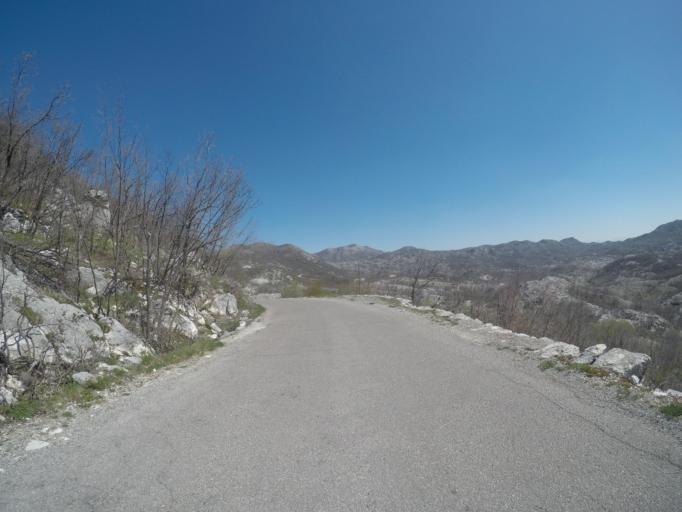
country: ME
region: Cetinje
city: Cetinje
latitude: 42.4373
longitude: 18.8705
